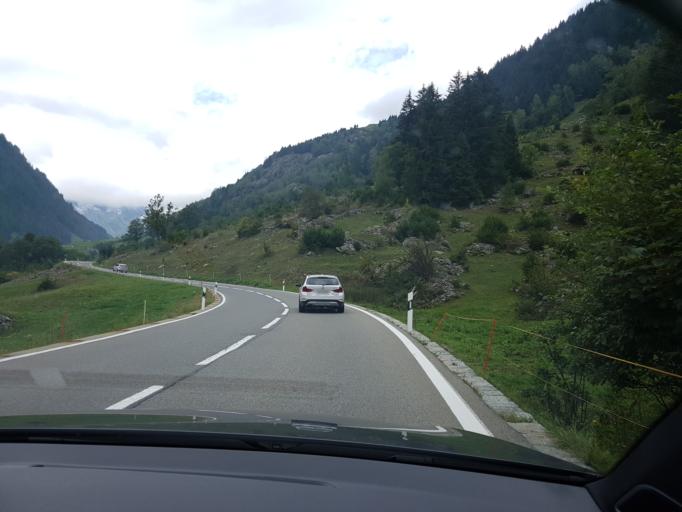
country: CH
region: Uri
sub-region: Uri
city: Andermatt
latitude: 46.7199
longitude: 8.5713
